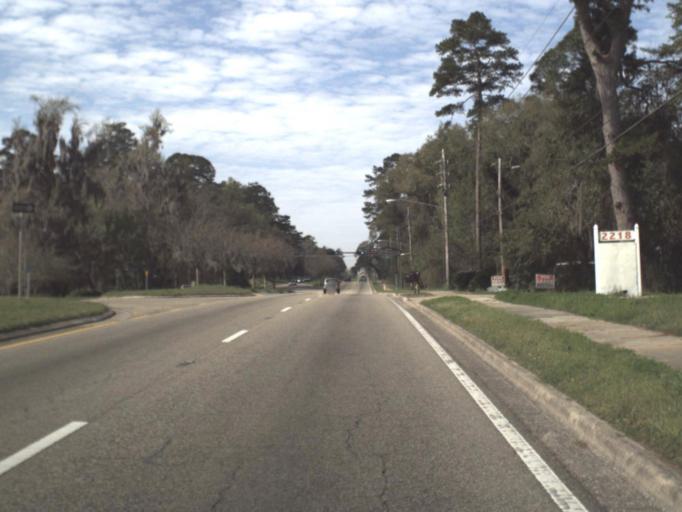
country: US
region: Florida
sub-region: Leon County
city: Tallahassee
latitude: 30.4551
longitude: -84.2420
